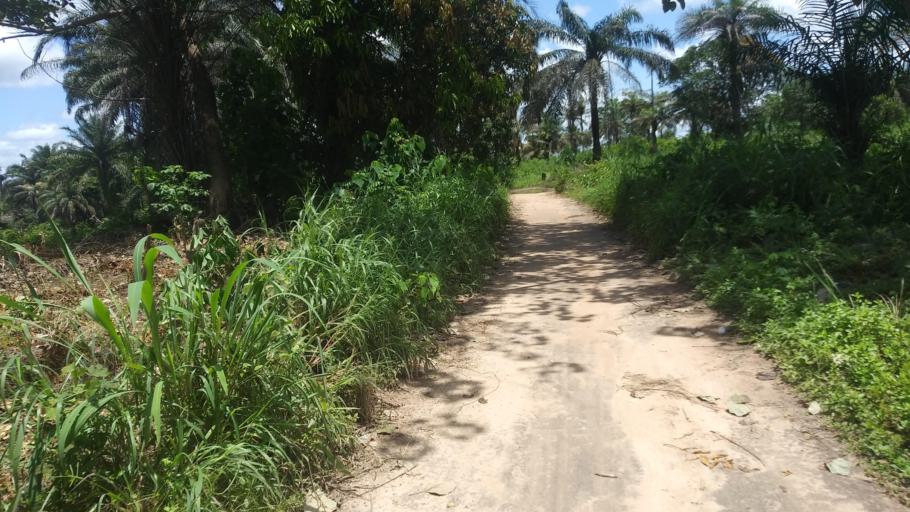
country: SL
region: Northern Province
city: Makeni
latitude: 8.8811
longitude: -12.0187
